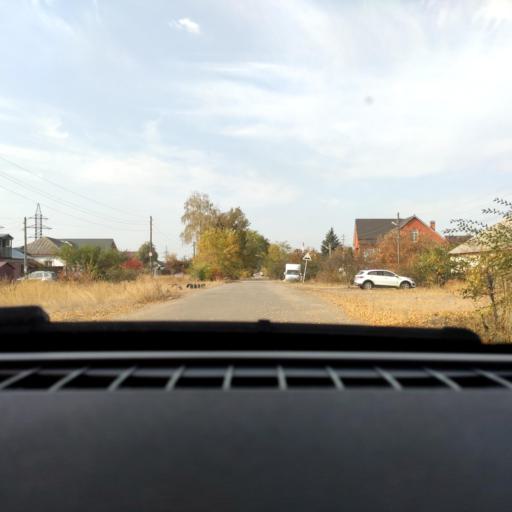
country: RU
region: Voronezj
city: Maslovka
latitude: 51.6290
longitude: 39.2820
